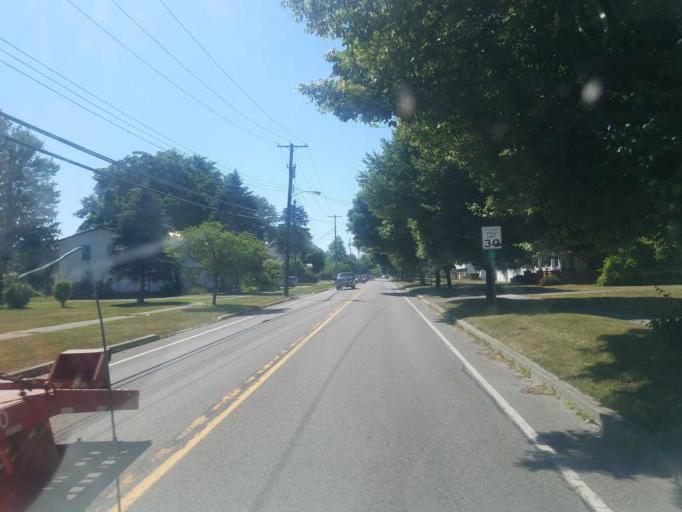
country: US
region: New York
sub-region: Ontario County
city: Phelps
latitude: 42.9615
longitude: -77.0714
